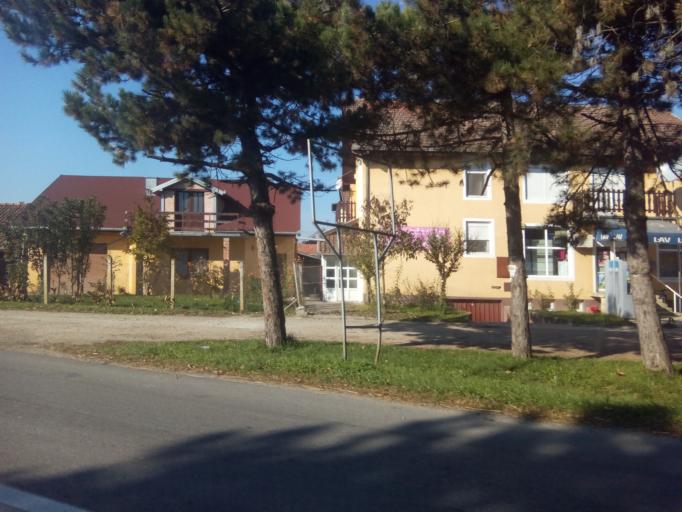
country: RS
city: Celarevo
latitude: 45.2713
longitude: 19.5349
